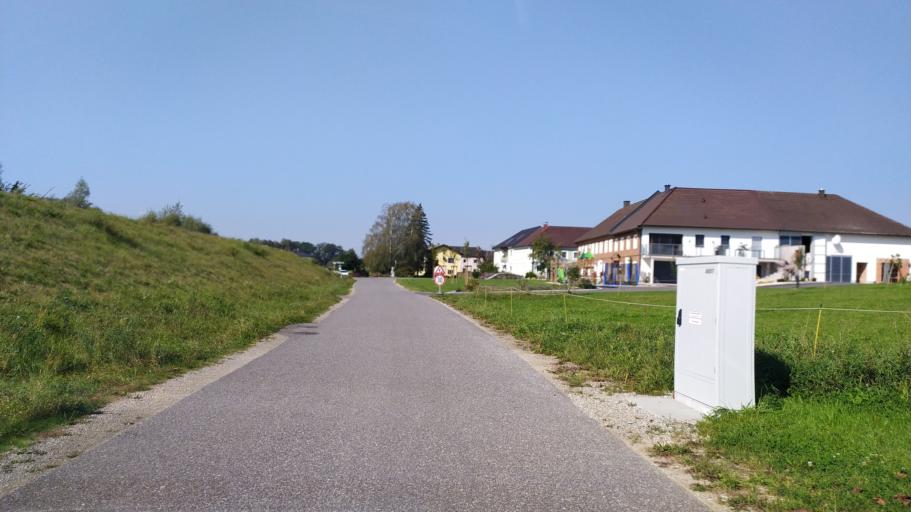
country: AT
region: Upper Austria
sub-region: Politischer Bezirk Perg
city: Perg
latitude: 48.1936
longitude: 14.7074
